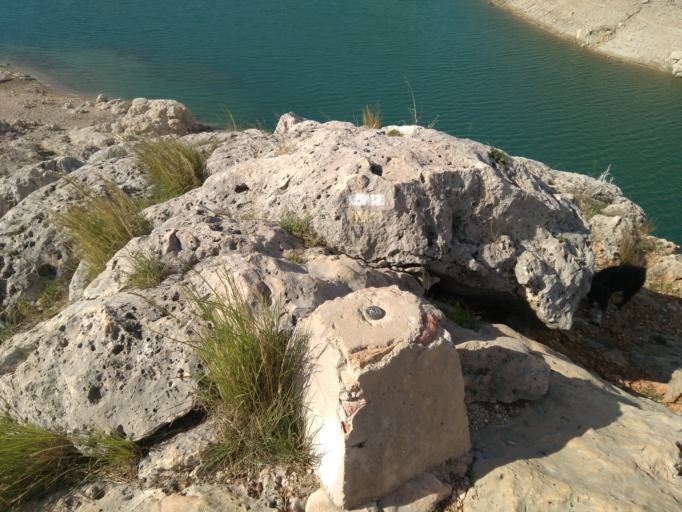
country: ES
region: Valencia
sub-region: Provincia de Valencia
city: Sumacarcer
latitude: 39.1572
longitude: -0.6601
